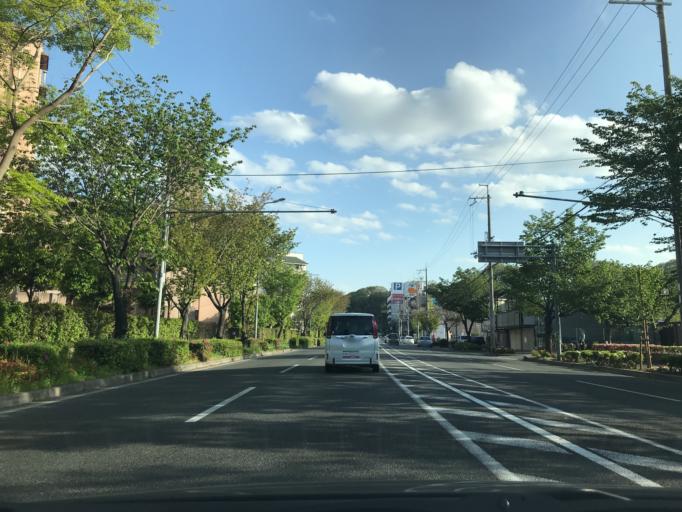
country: JP
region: Osaka
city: Ikeda
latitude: 34.8575
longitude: 135.4167
